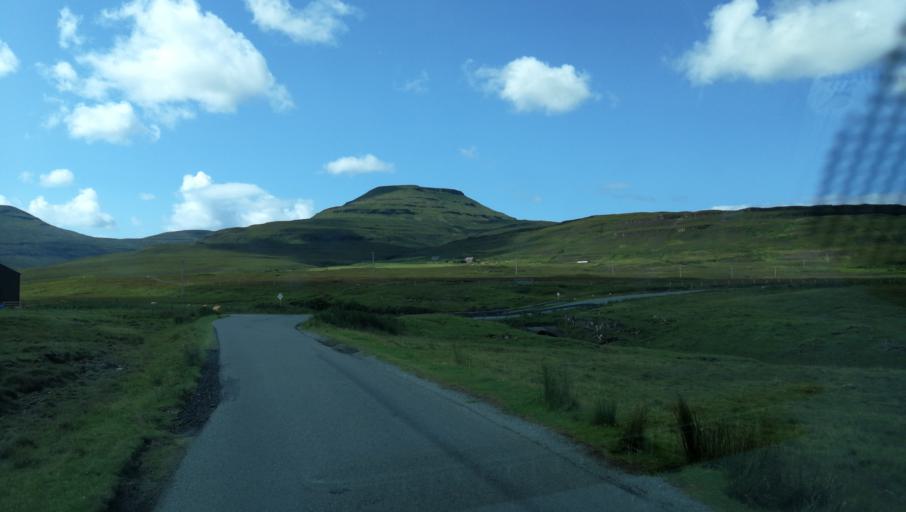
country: GB
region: Scotland
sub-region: Highland
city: Isle of Skye
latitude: 57.4211
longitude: -6.5838
